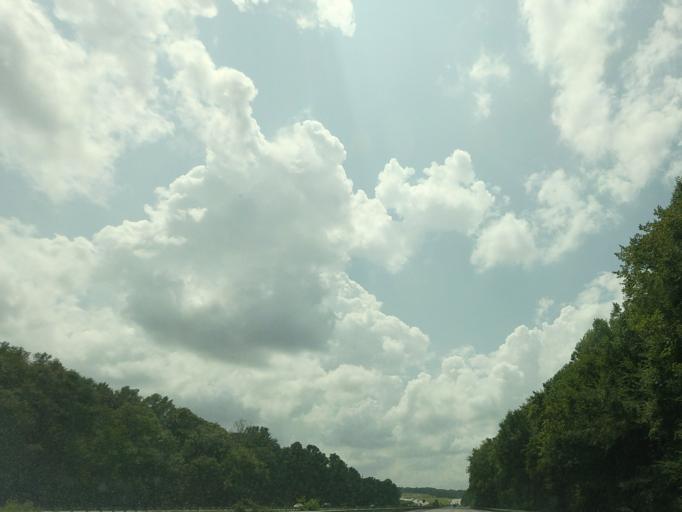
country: US
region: Georgia
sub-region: Bibb County
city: West Point
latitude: 32.7688
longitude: -83.7110
